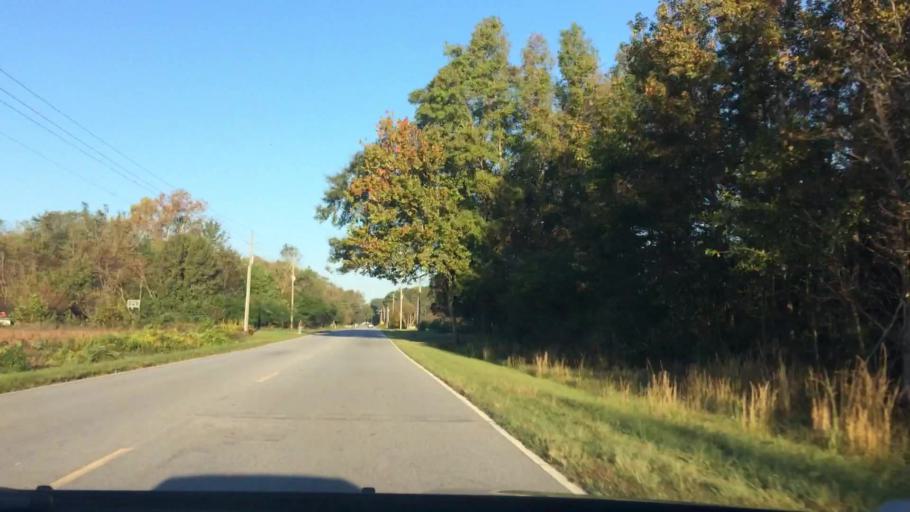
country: US
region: North Carolina
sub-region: Pitt County
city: Grifton
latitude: 35.4037
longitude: -77.4171
